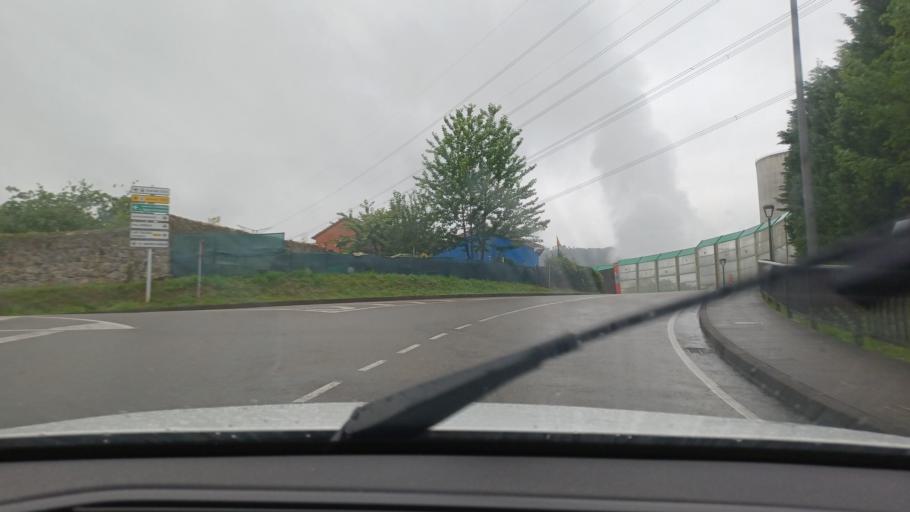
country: ES
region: Asturias
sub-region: Province of Asturias
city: Castandiello
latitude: 43.3106
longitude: -5.8744
